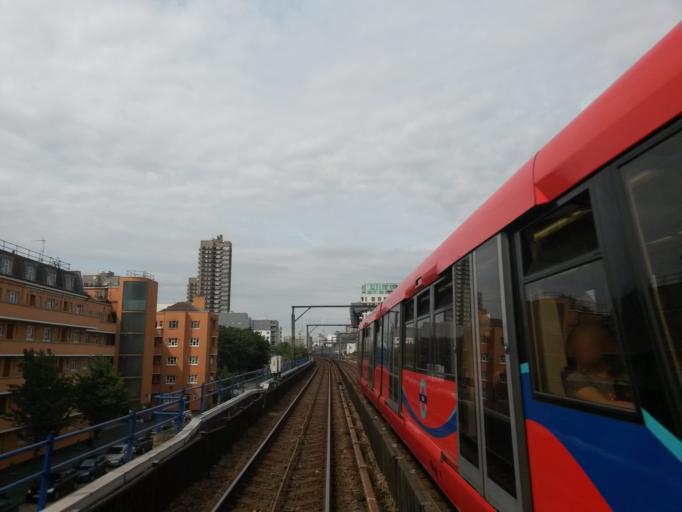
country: GB
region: England
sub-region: Greater London
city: Bethnal Green
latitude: 51.5115
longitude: -0.0594
